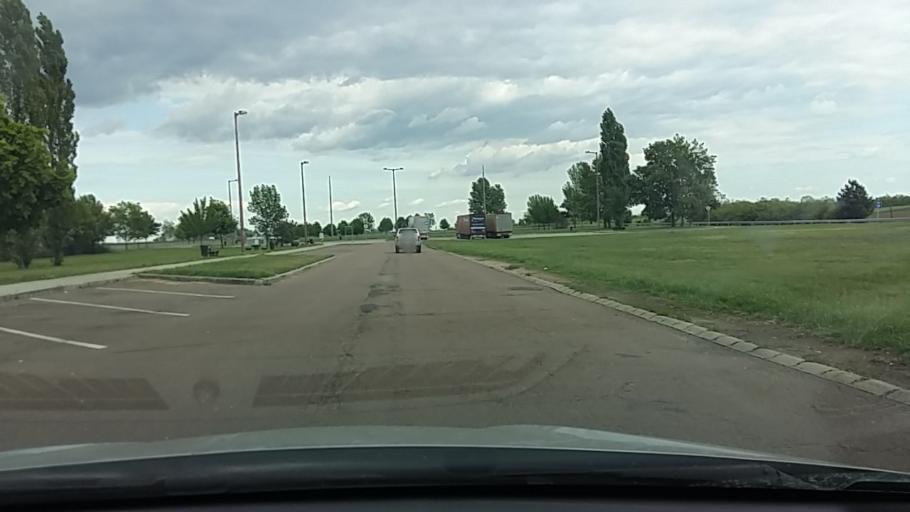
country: HU
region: Heves
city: Erdotelek
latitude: 47.7222
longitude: 20.3165
